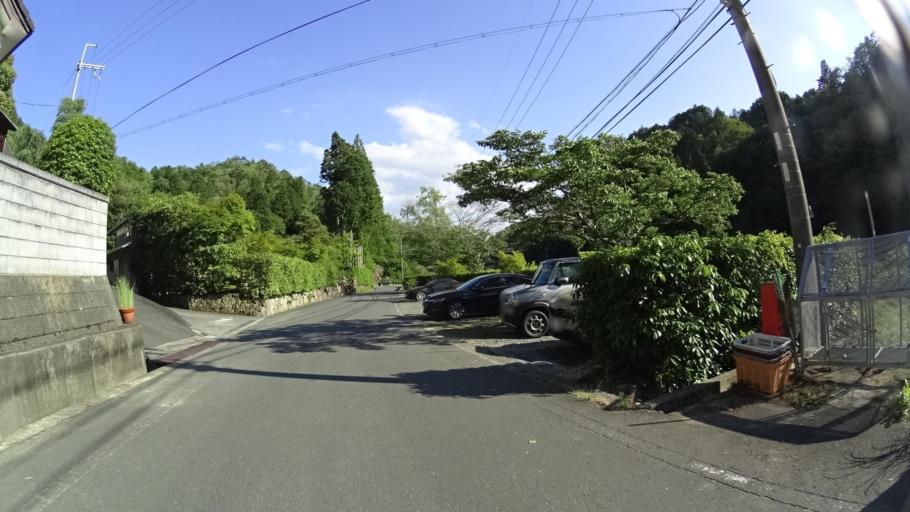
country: JP
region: Kyoto
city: Kameoka
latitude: 34.9734
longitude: 135.5616
